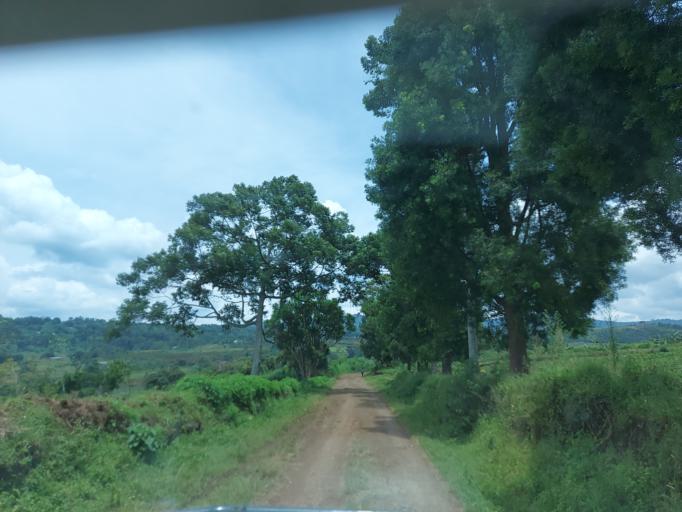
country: CD
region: South Kivu
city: Kabare
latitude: -2.3382
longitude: 28.7871
